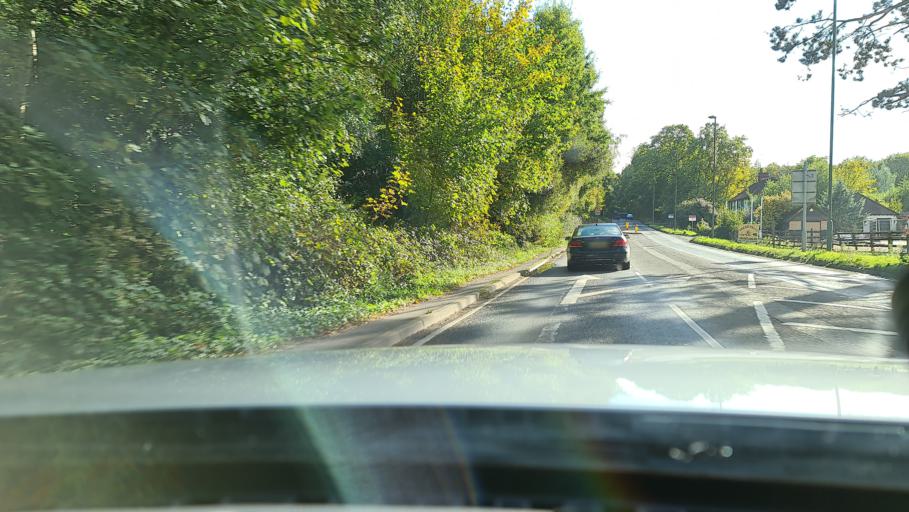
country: GB
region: England
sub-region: Surrey
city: Weybridge
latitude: 51.3536
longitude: -0.4342
